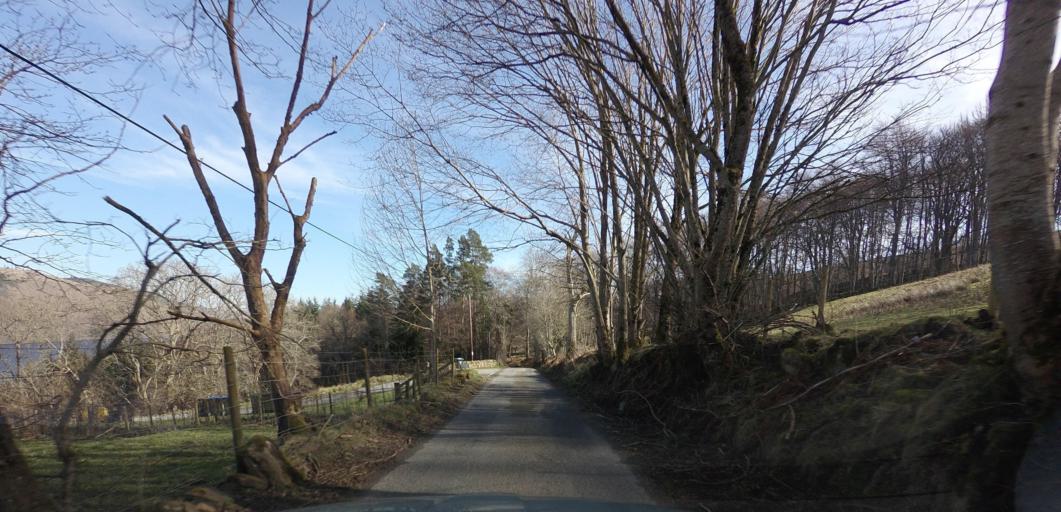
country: GB
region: Scotland
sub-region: Perth and Kinross
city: Comrie
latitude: 56.5622
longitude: -4.0542
